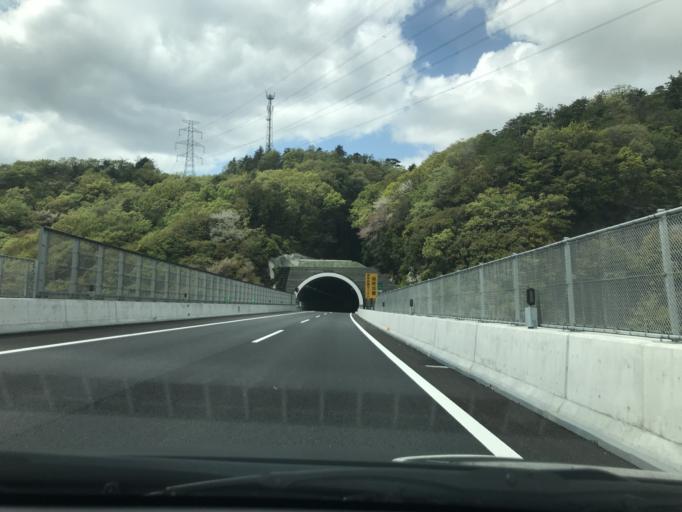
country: JP
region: Osaka
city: Ikeda
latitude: 34.8754
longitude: 135.4205
